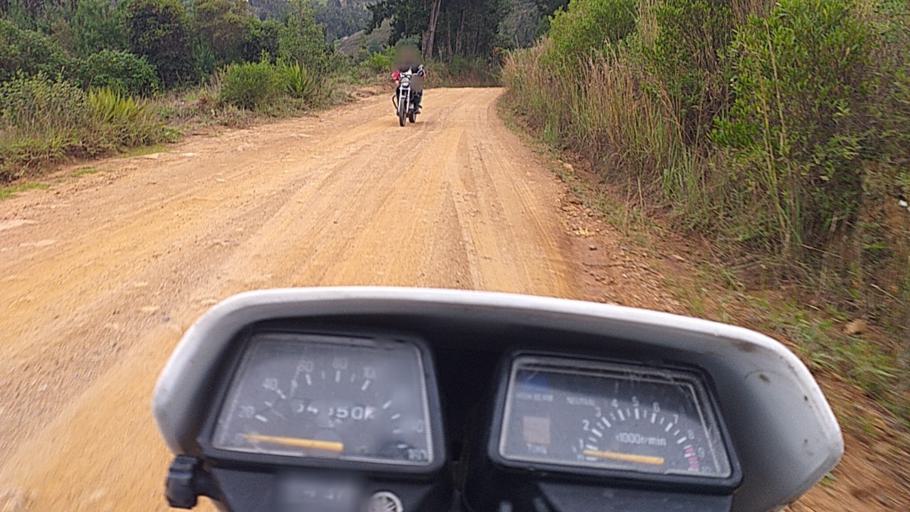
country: CO
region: Boyaca
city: Floresta
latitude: 5.8755
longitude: -72.9137
